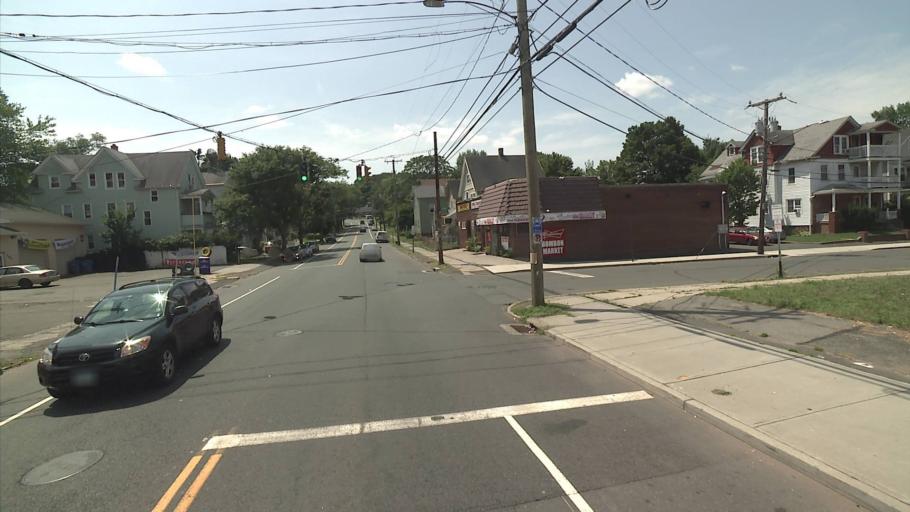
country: US
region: Connecticut
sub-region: New Haven County
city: Meriden
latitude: 41.5304
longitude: -72.8086
